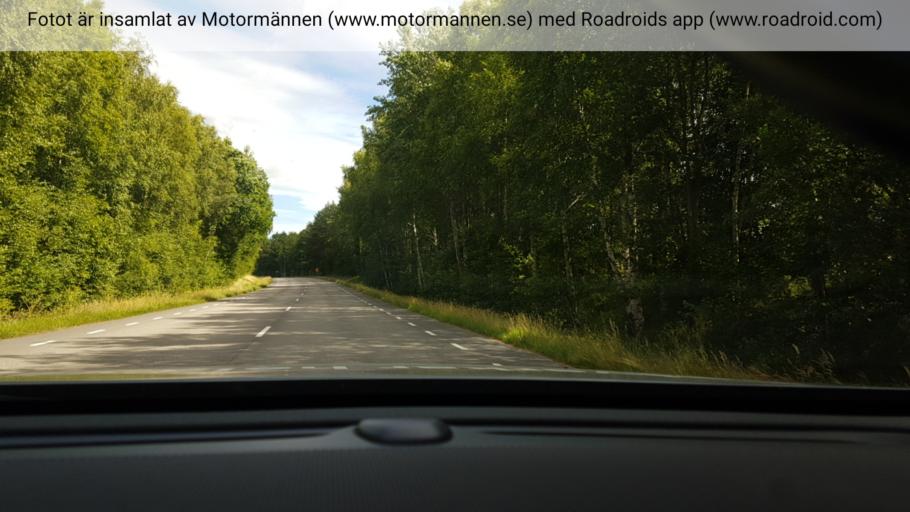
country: SE
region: Skane
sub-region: Hassleholms Kommun
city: Hassleholm
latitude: 56.1770
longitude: 13.7857
